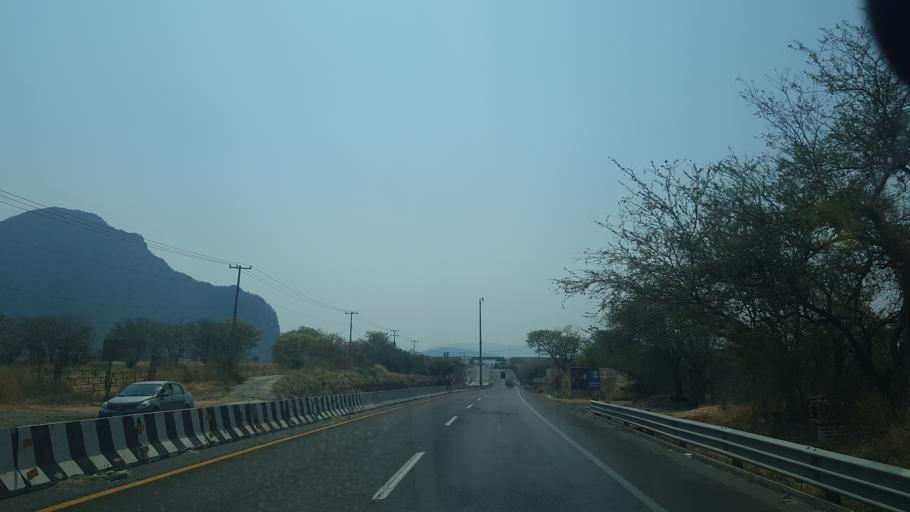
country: MX
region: Morelos
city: Jantetelco
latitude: 18.7065
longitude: -98.7745
